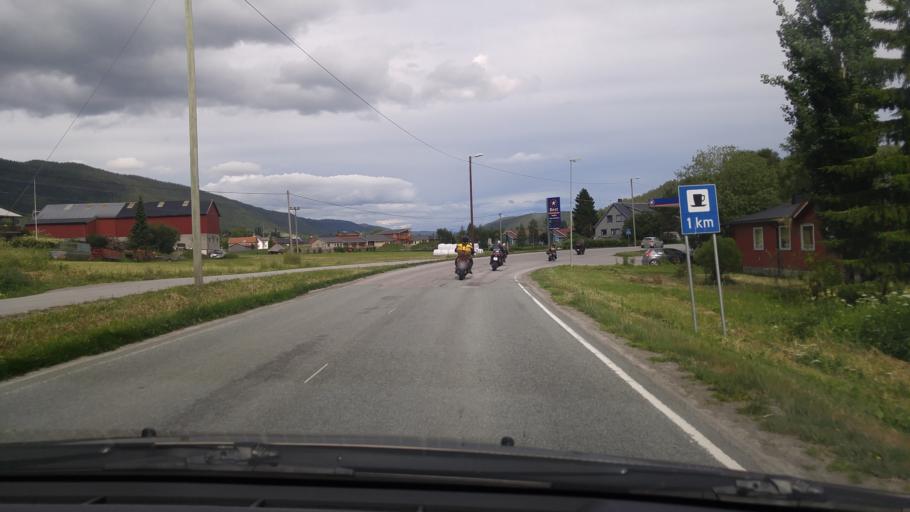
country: NO
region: Nord-Trondelag
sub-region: Steinkjer
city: Steinkjer
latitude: 64.1120
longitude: 11.3803
